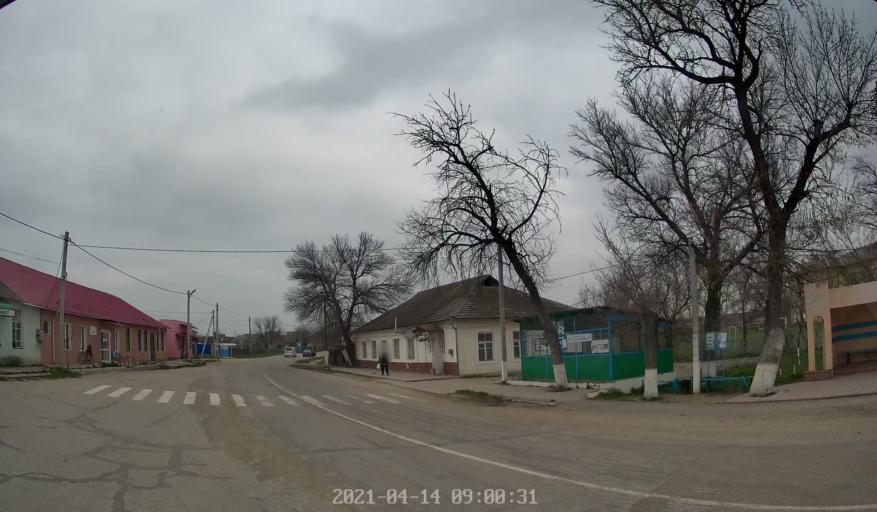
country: MD
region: Chisinau
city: Vadul lui Voda
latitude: 47.0994
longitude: 29.1121
